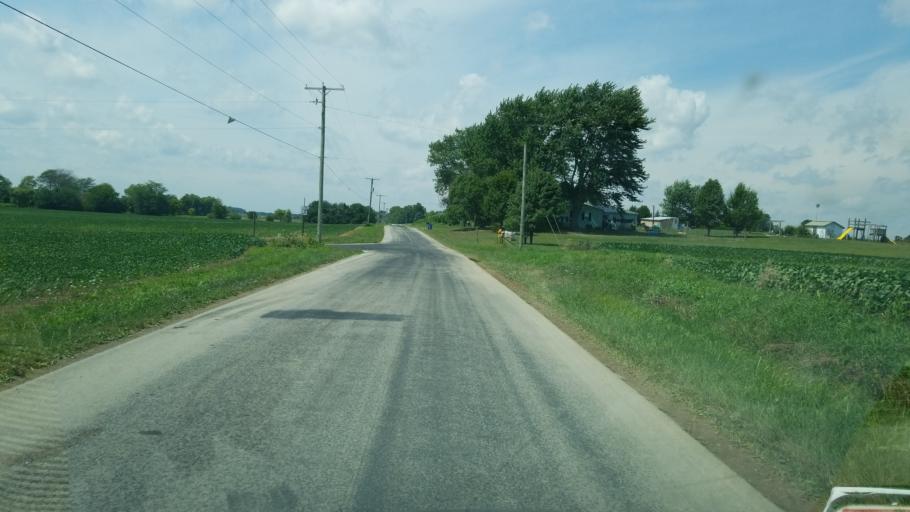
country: US
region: Ohio
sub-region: Hardin County
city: Forest
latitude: 40.8710
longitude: -83.5051
